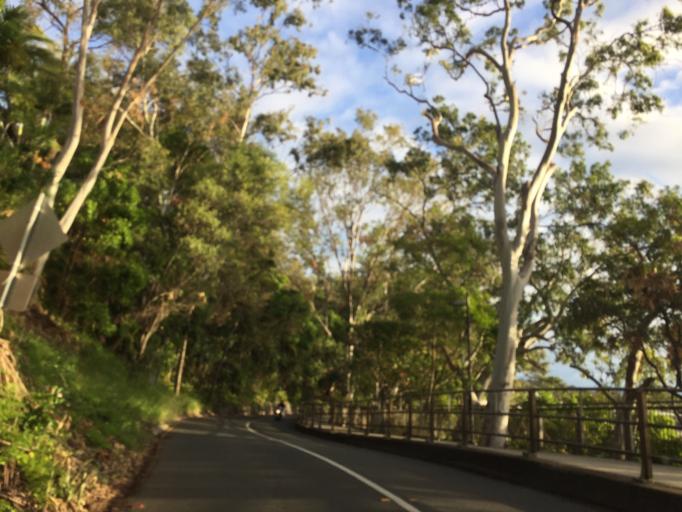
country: AU
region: Queensland
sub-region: Sunshine Coast
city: Noosa Heads
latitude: -26.3850
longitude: 153.0947
